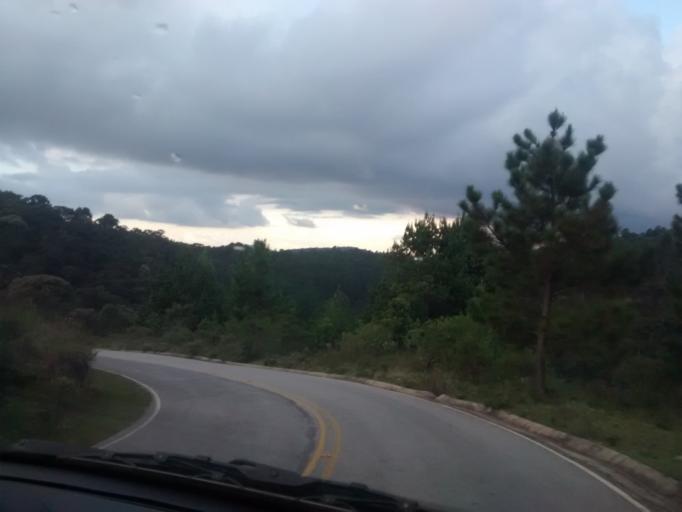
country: BR
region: Sao Paulo
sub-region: Campos Do Jordao
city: Campos do Jordao
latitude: -22.6537
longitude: -45.6244
